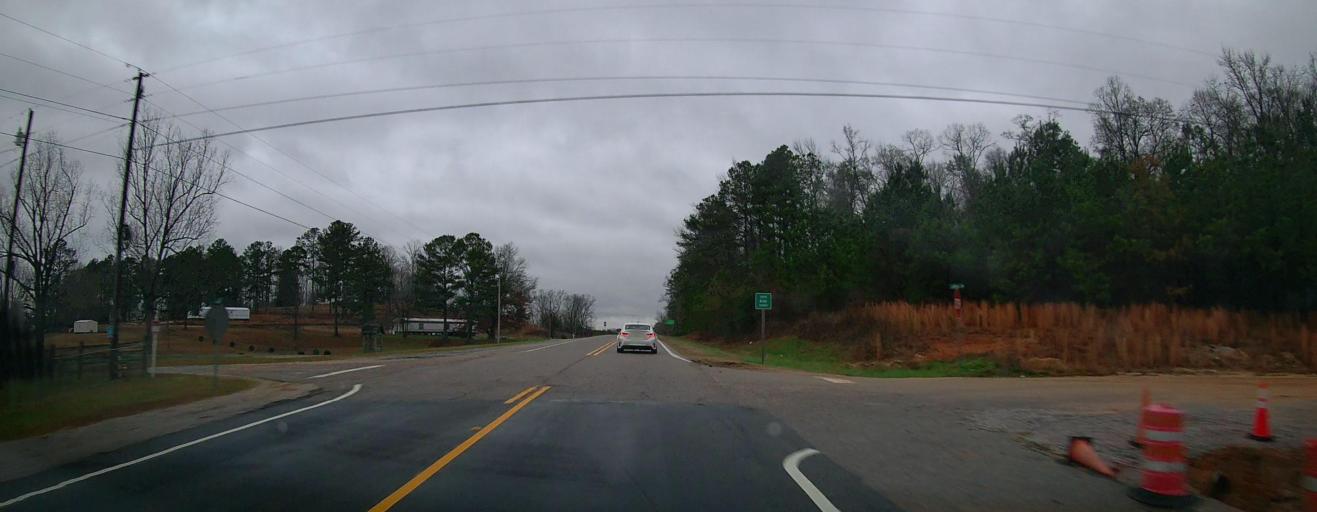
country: US
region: Alabama
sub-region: Bibb County
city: Centreville
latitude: 32.8373
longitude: -86.9557
